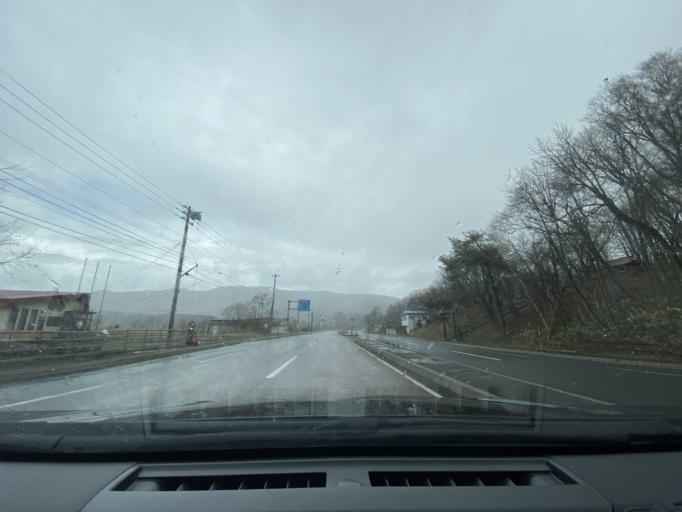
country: JP
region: Hokkaido
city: Fukagawa
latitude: 43.7263
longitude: 142.1867
